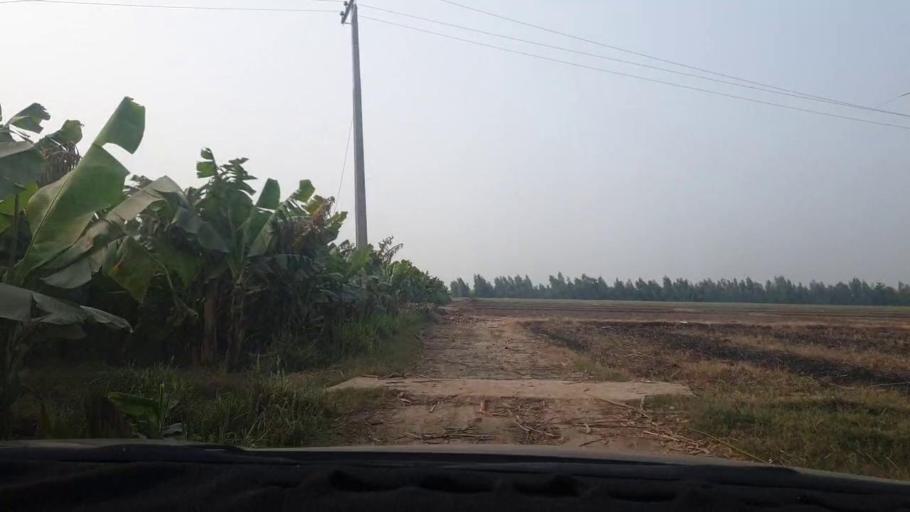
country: PK
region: Sindh
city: Matiari
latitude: 25.6022
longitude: 68.5485
